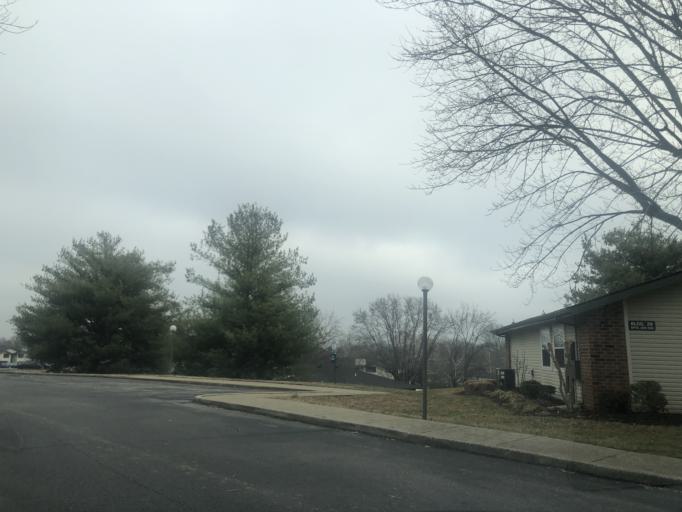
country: US
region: Tennessee
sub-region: Rutherford County
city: La Vergne
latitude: 36.0673
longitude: -86.6421
